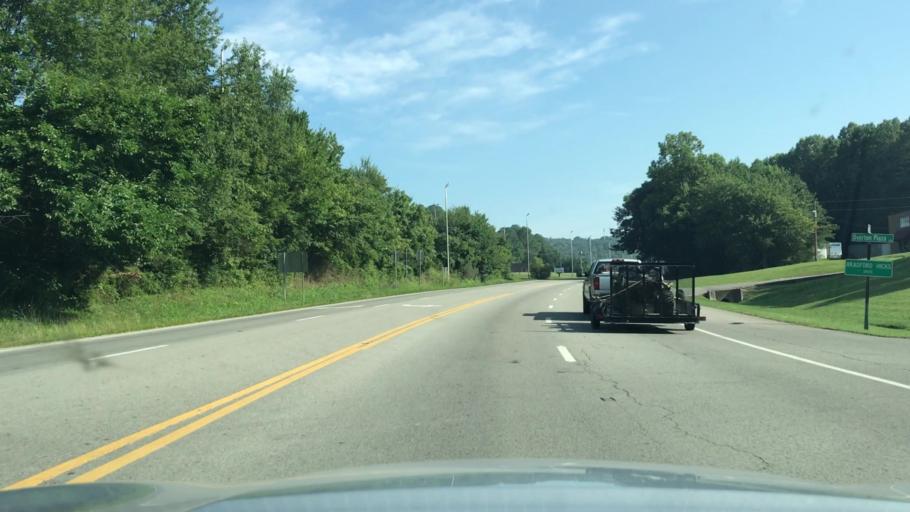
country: US
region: Tennessee
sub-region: Overton County
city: Livingston
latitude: 36.3795
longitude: -85.3346
